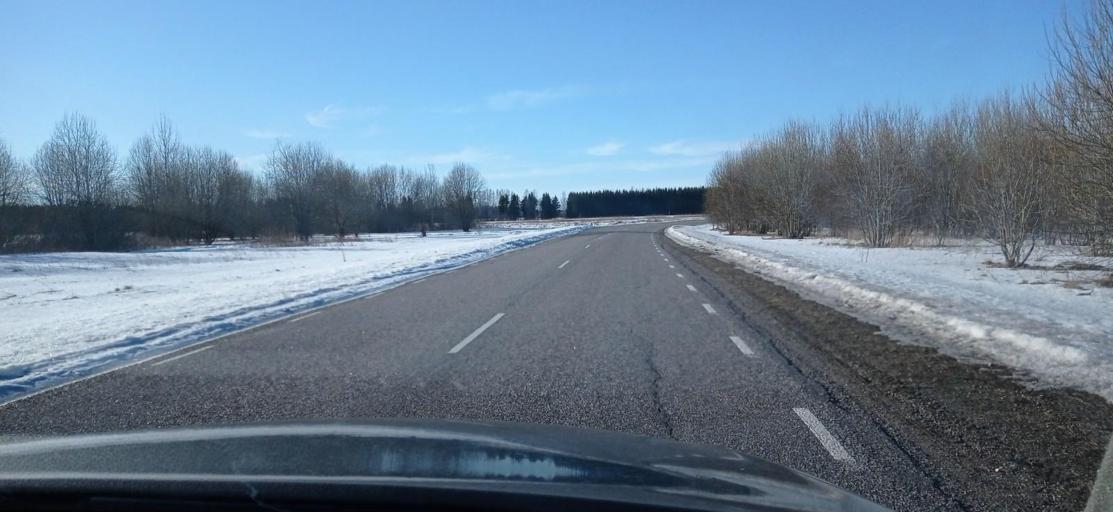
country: EE
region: Tartu
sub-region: Alatskivi vald
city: Kallaste
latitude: 58.4921
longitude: 27.2334
